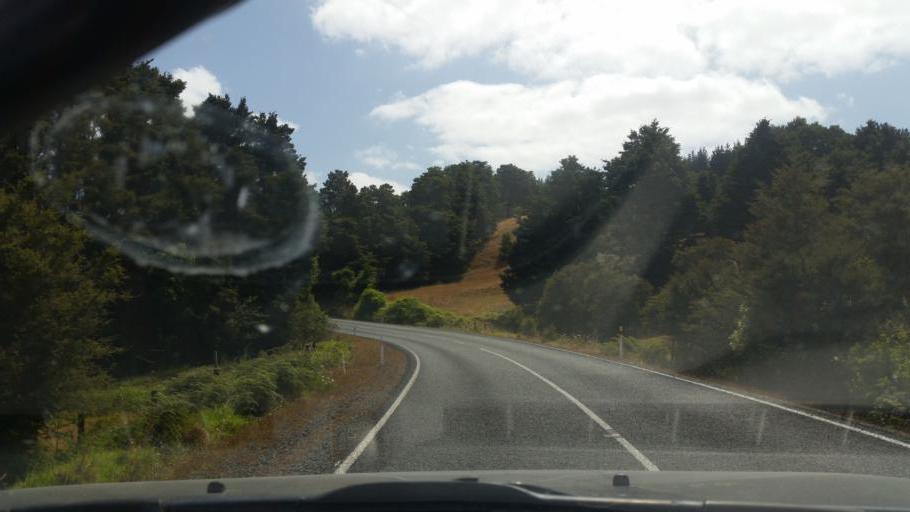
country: NZ
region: Northland
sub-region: Whangarei
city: Ruakaka
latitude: -35.9423
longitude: 174.2923
